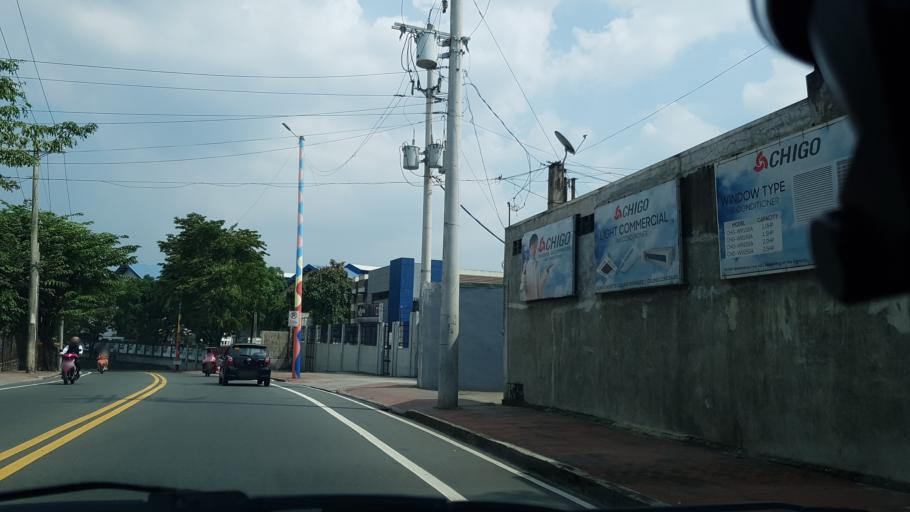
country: PH
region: Calabarzon
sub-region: Province of Rizal
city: San Mateo
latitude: 14.6629
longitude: 121.1192
